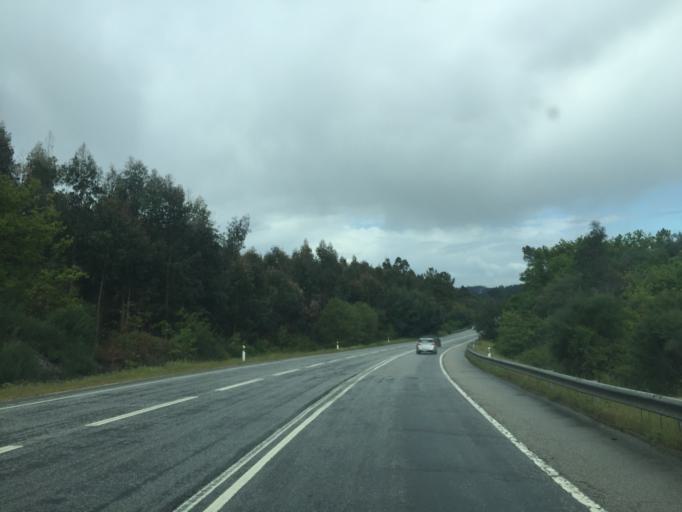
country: PT
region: Viseu
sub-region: Viseu
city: Abraveses
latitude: 40.6597
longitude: -8.0128
